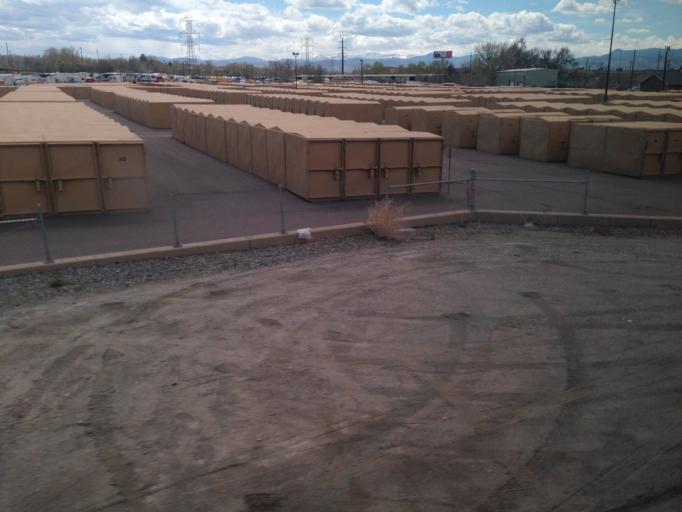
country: US
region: Colorado
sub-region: Adams County
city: Berkley
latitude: 39.8067
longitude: -105.0085
